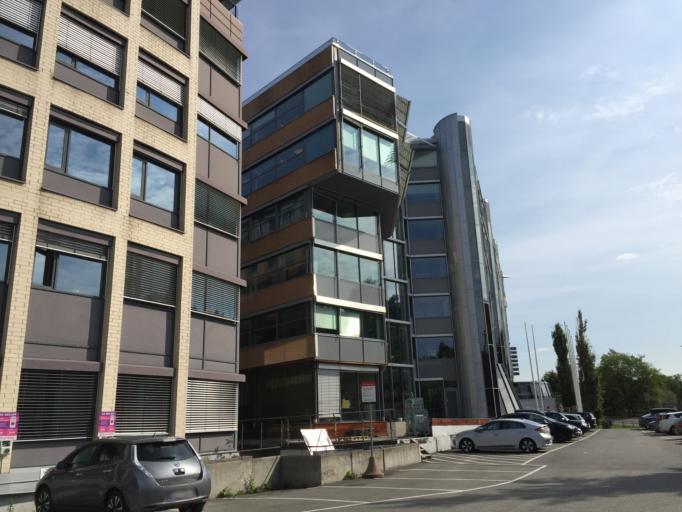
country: NO
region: Oslo
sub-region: Oslo
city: Sjolyststranda
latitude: 59.9184
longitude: 10.6846
